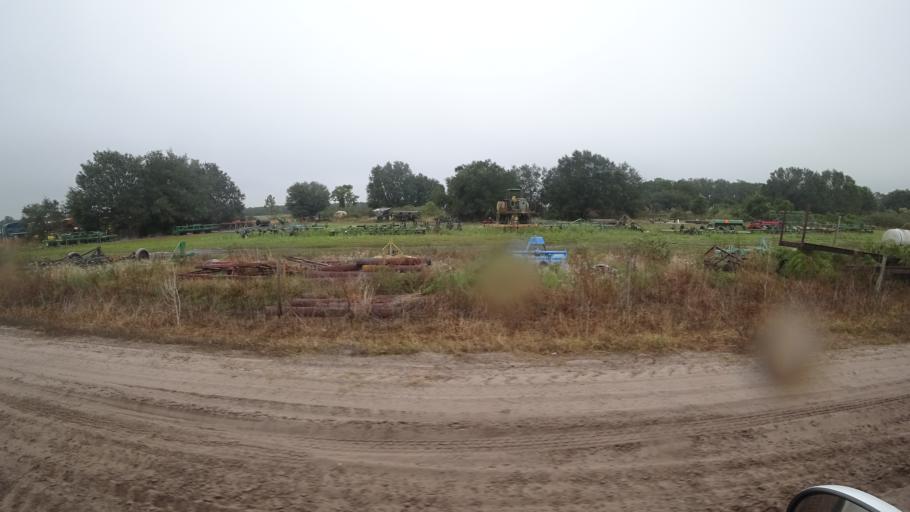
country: US
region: Florida
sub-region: Sarasota County
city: Warm Mineral Springs
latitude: 27.2809
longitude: -82.1686
